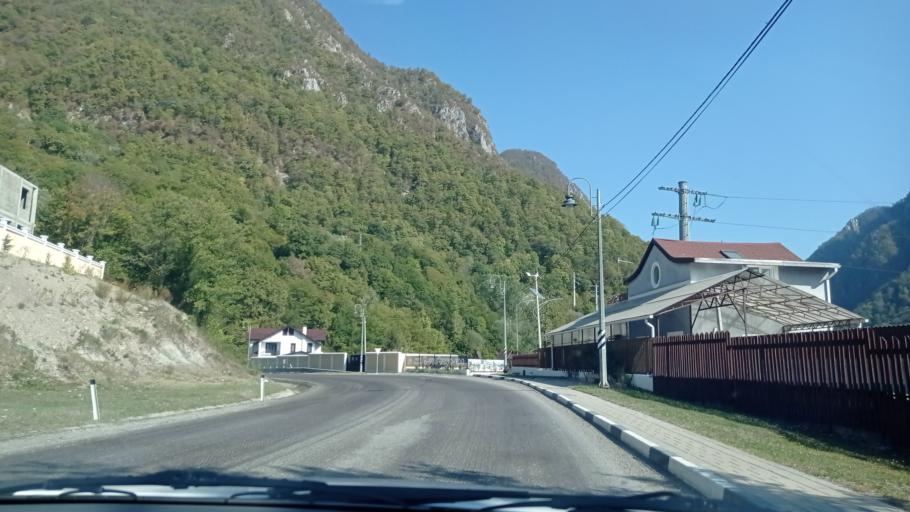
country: RU
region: Krasnodarskiy
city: Vysokoye
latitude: 43.5914
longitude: 40.0077
